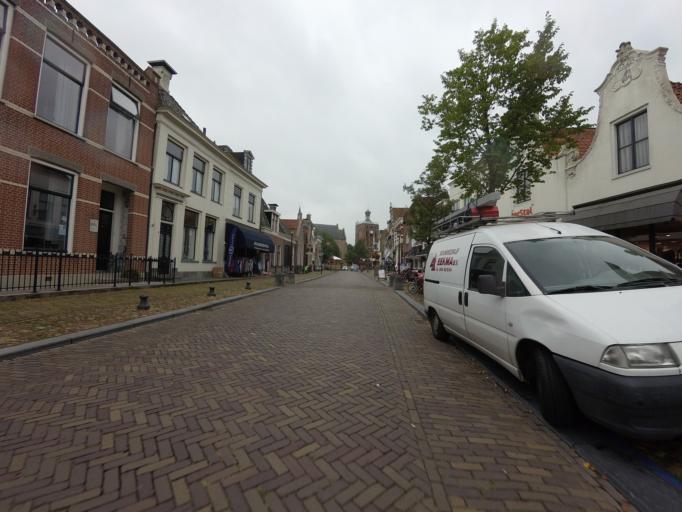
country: NL
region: Friesland
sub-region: Sudwest Fryslan
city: Workum
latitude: 52.9803
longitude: 5.4440
